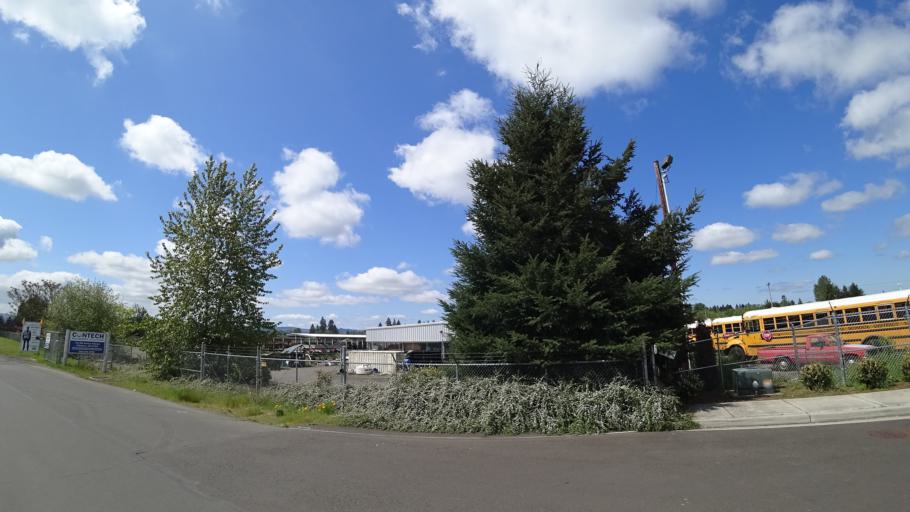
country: US
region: Oregon
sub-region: Washington County
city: Hillsboro
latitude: 45.5153
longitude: -123.0011
